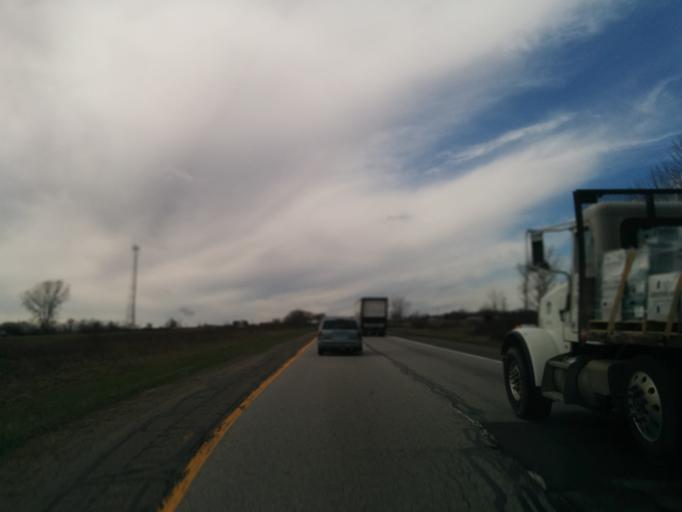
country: US
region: Michigan
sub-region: Ottawa County
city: Hudsonville
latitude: 42.8294
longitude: -85.9186
